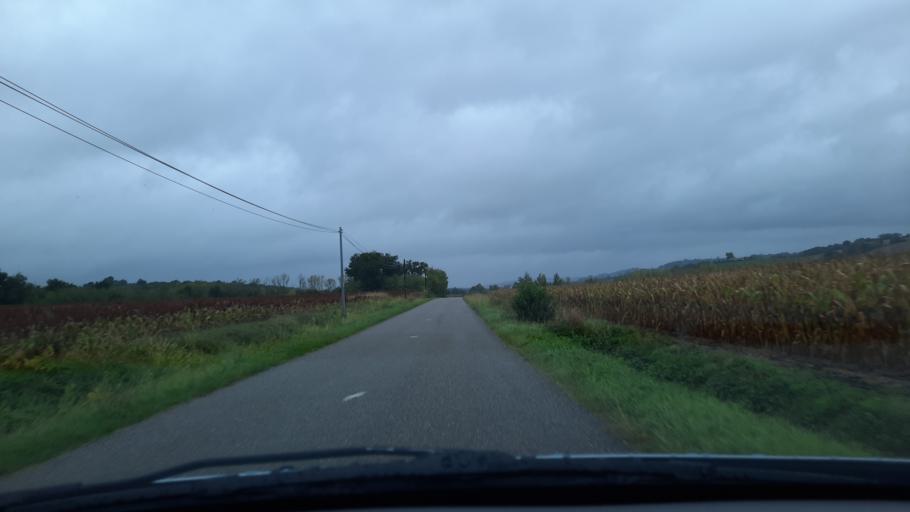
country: FR
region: Midi-Pyrenees
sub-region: Departement du Tarn-et-Garonne
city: Lafrancaise
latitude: 44.1785
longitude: 1.2691
